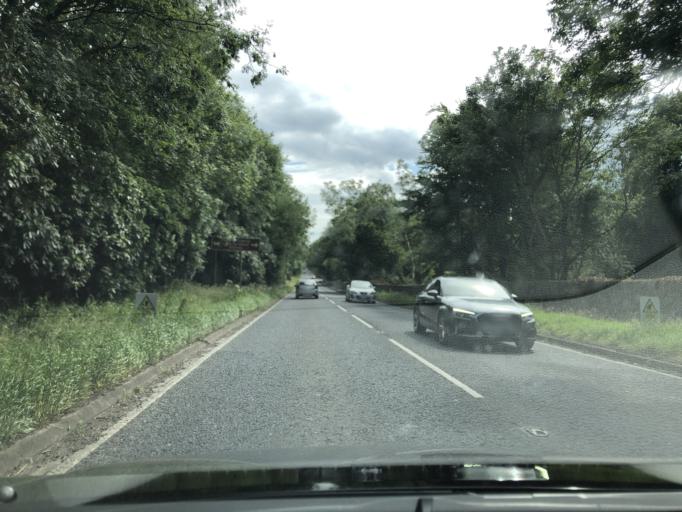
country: GB
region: Northern Ireland
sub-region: Down District
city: Dundrum
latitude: 54.3176
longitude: -5.8386
